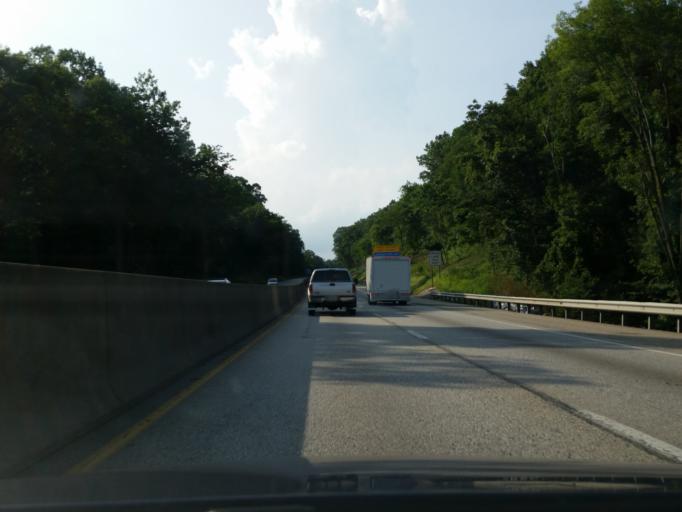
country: US
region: Pennsylvania
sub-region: York County
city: Valley Green
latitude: 40.1044
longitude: -76.7798
